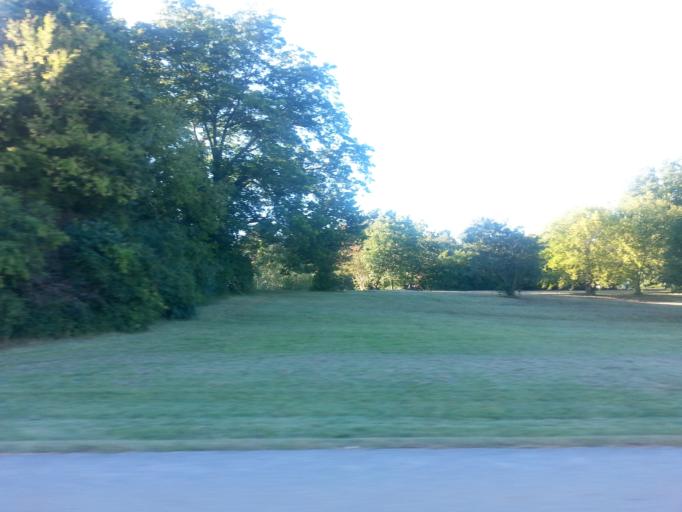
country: US
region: Tennessee
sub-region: Blount County
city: Alcoa
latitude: 35.8238
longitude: -83.9897
